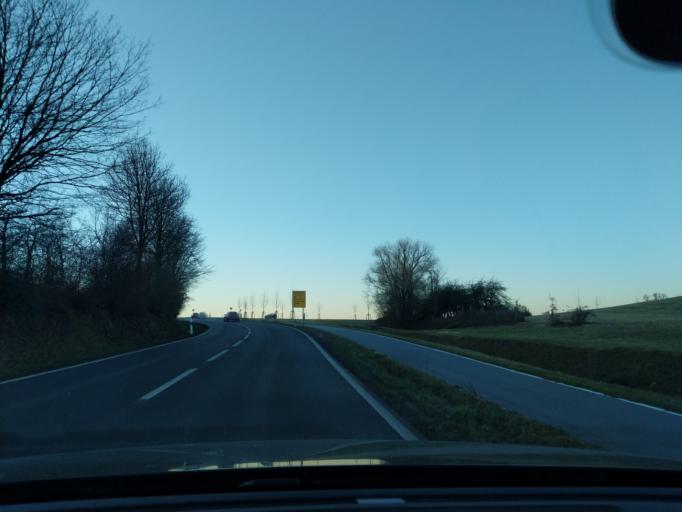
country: DE
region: Baden-Wuerttemberg
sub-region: Tuebingen Region
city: Bermatingen
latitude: 47.7280
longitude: 9.3164
